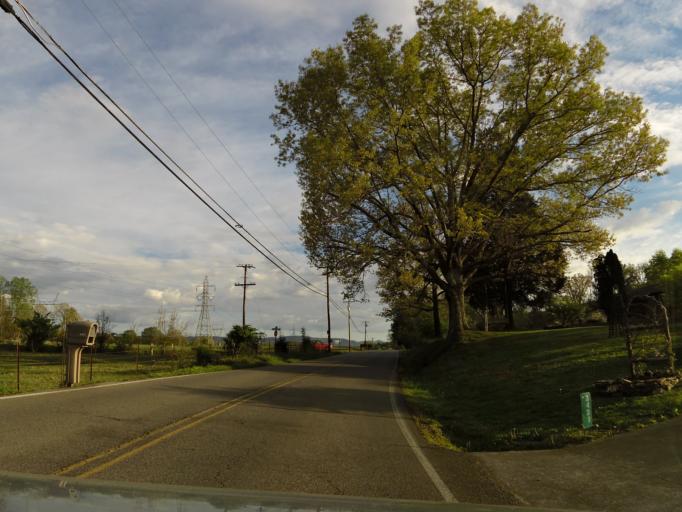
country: US
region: Tennessee
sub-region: Blount County
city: Maryville
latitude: 35.6808
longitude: -84.0124
